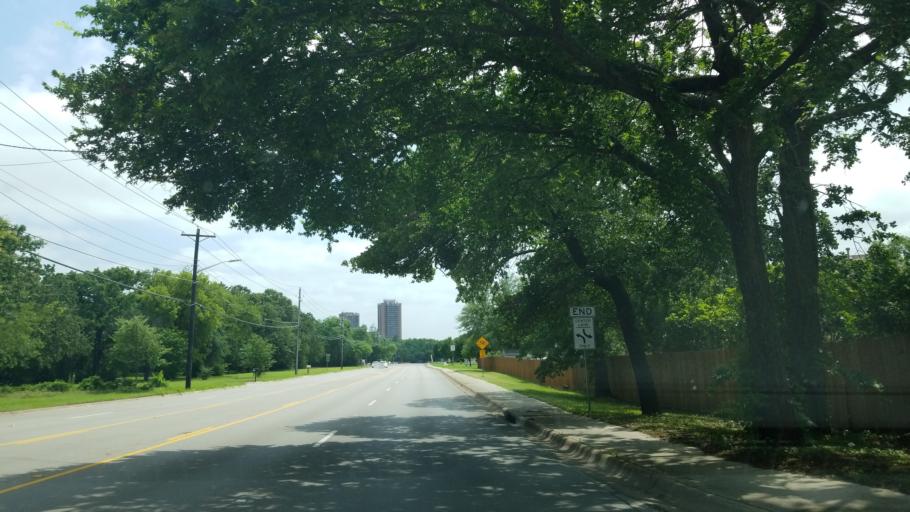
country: US
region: Texas
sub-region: Denton County
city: Denton
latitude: 33.2390
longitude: -97.1227
